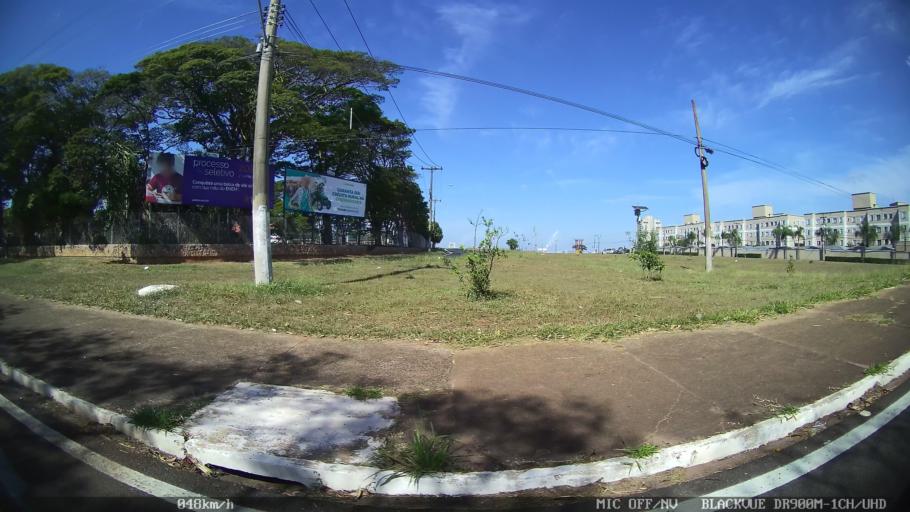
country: BR
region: Sao Paulo
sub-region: Franca
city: Franca
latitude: -20.5416
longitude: -47.4196
